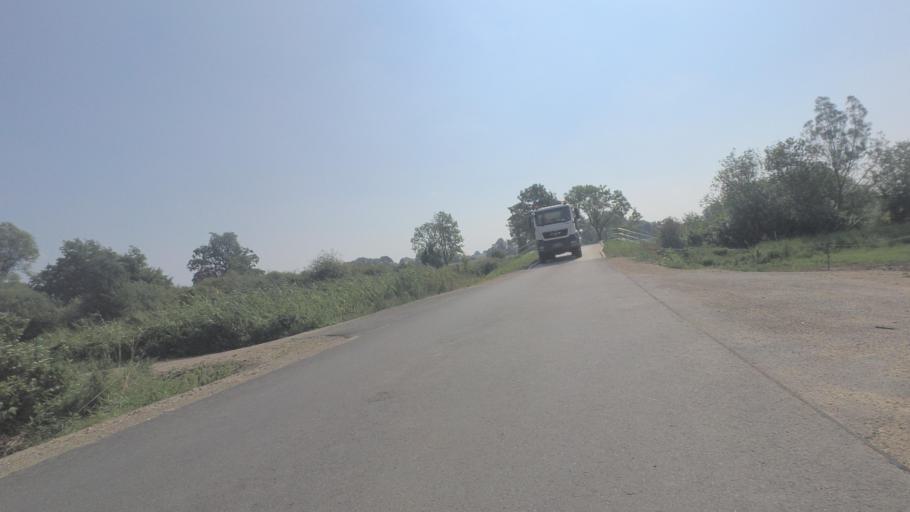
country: DE
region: Mecklenburg-Vorpommern
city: Gielow
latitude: 53.7240
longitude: 12.6798
